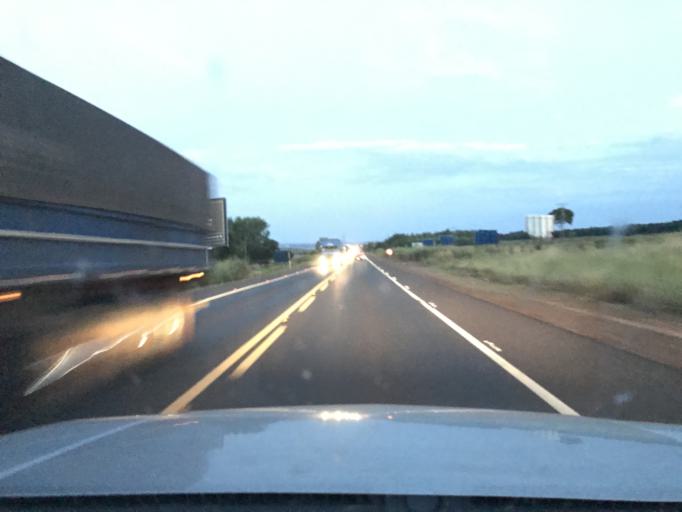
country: PY
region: Canindeyu
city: Salto del Guaira
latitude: -24.0139
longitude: -54.3005
